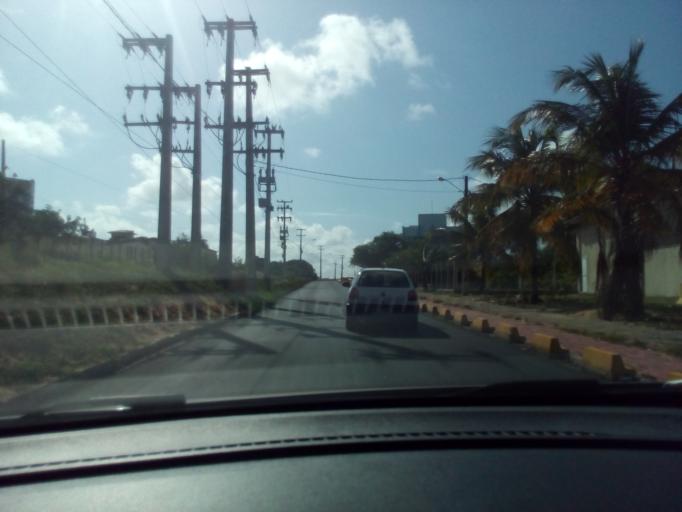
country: BR
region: Rio Grande do Norte
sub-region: Natal
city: Natal
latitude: -5.8436
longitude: -35.2007
